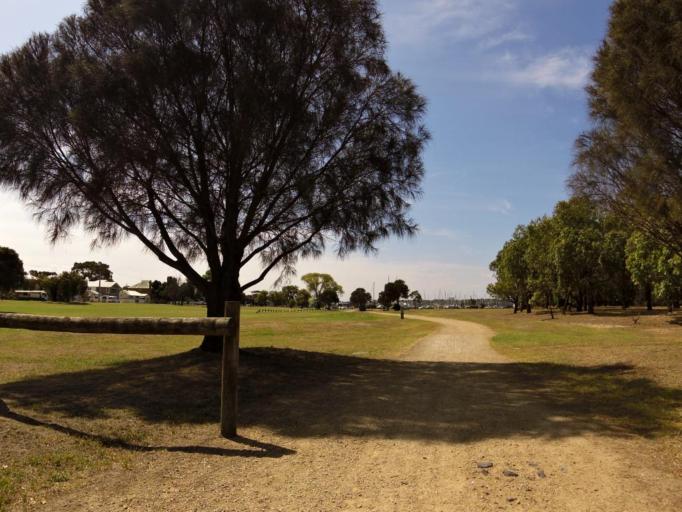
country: AU
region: Victoria
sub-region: Mornington Peninsula
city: Hastings
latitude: -38.3119
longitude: 145.1958
